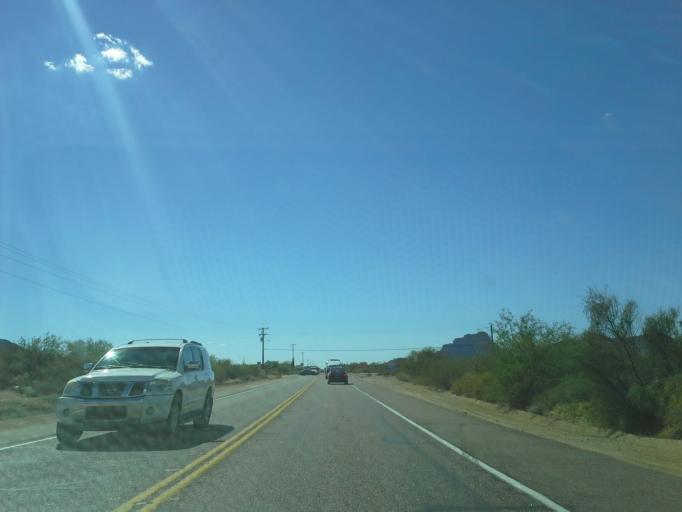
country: US
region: Arizona
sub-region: Maricopa County
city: Fountain Hills
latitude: 33.5443
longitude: -111.6090
